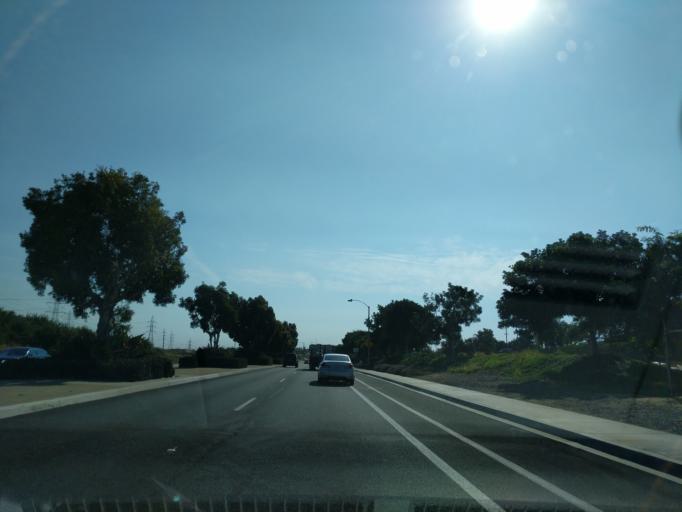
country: US
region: California
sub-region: San Diego County
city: Carlsbad
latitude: 33.1346
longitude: -117.3198
